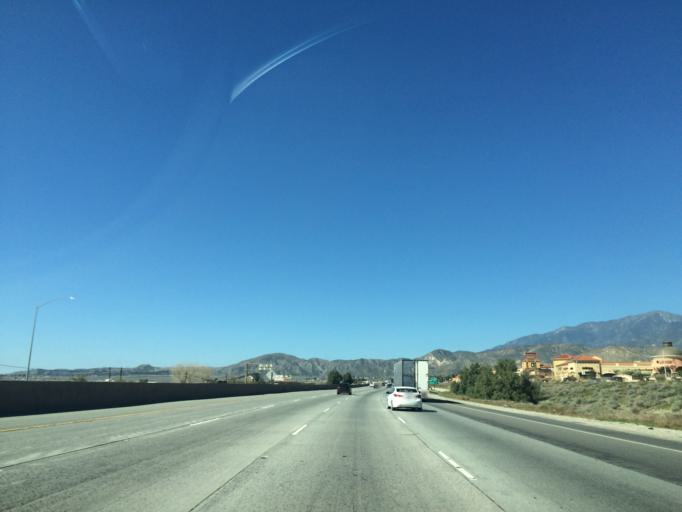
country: US
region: California
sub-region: Riverside County
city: Cabazon
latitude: 33.9233
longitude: -116.8101
